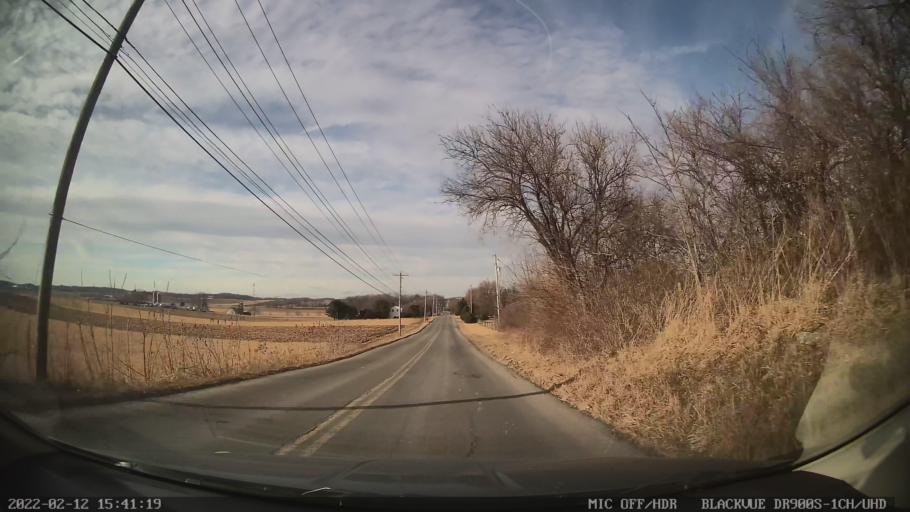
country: US
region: Pennsylvania
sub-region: Berks County
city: Topton
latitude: 40.5206
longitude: -75.7317
